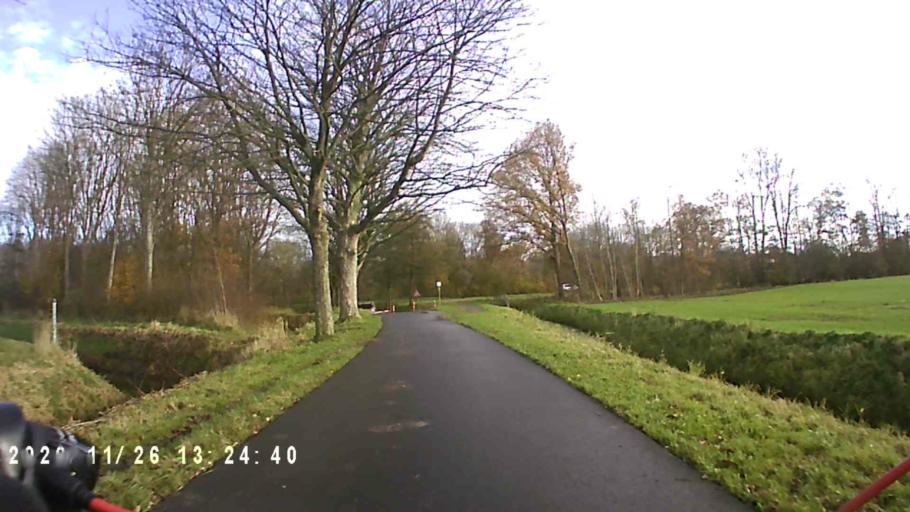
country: NL
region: Groningen
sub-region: Gemeente Delfzijl
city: Delfzijl
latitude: 53.3445
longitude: 6.9001
